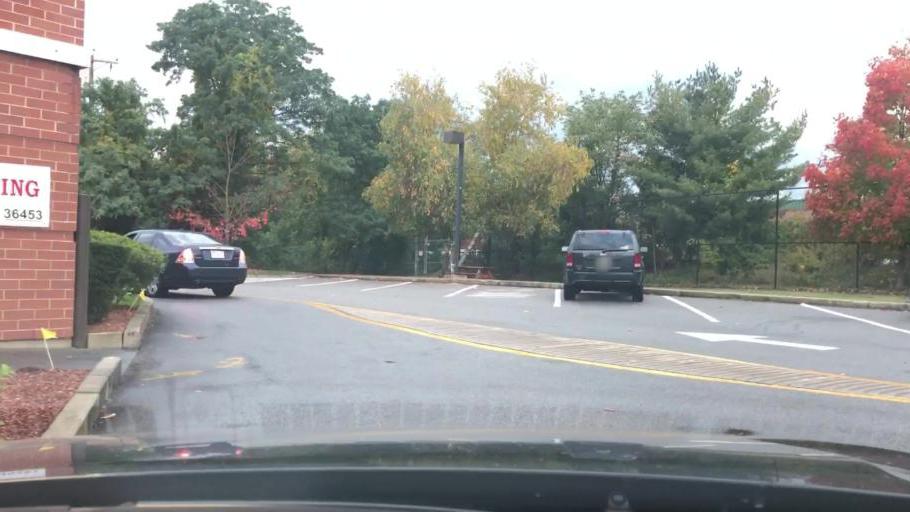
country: US
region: Massachusetts
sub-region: Middlesex County
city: Chelmsford
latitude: 42.6263
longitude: -71.3609
